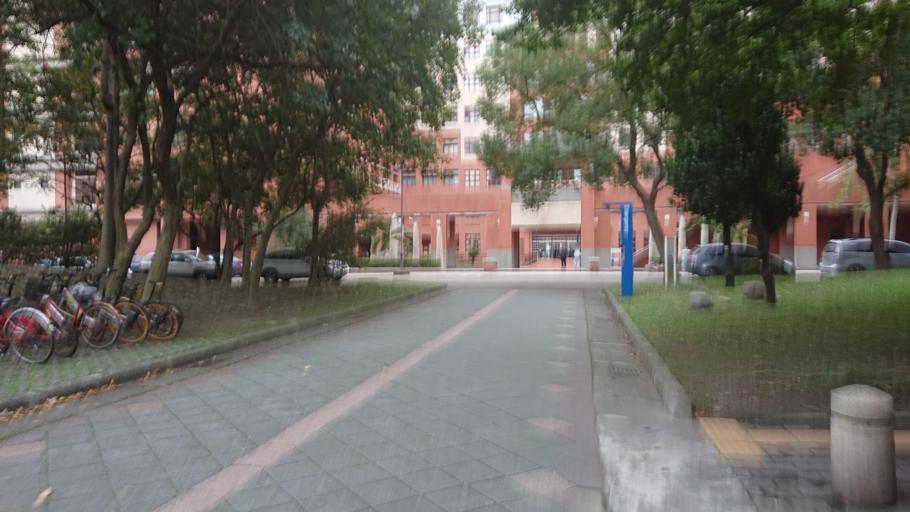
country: TW
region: Taiwan
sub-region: Taoyuan
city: Taoyuan
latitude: 24.9460
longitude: 121.3715
